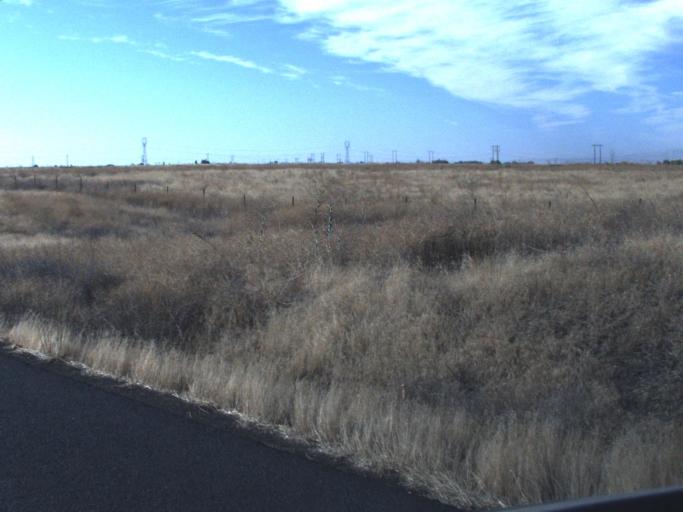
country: US
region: Washington
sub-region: Franklin County
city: Connell
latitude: 46.6552
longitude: -119.0064
